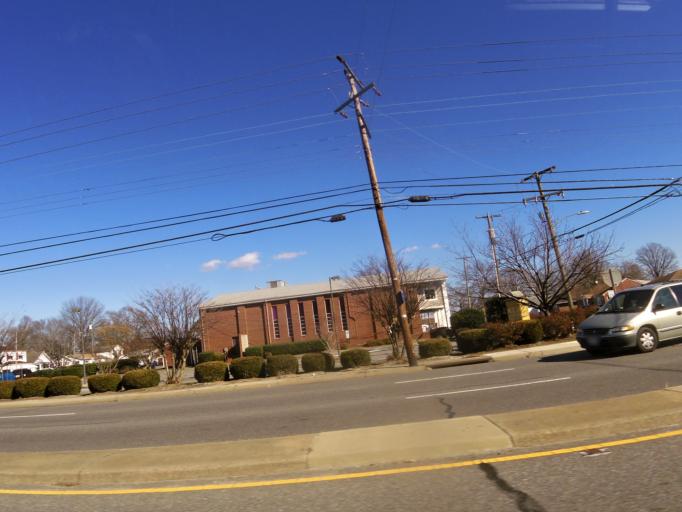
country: US
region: Virginia
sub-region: City of Newport News
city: Newport News
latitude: 36.9925
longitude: -76.4280
